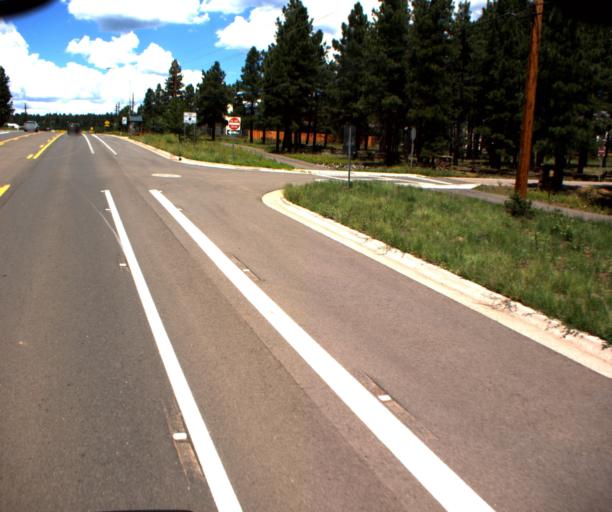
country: US
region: Arizona
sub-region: Coconino County
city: Flagstaff
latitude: 35.2352
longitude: -111.6652
